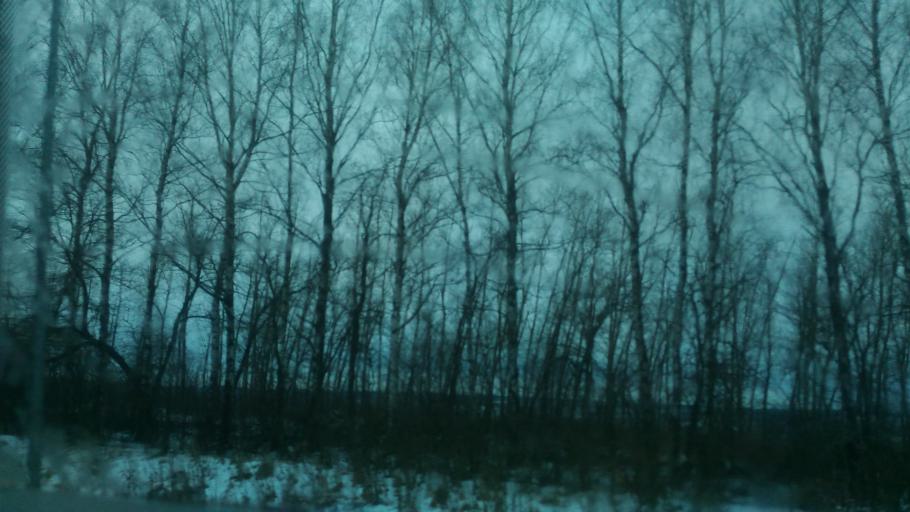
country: RU
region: Tula
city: Bolokhovo
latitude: 54.0890
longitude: 37.7738
